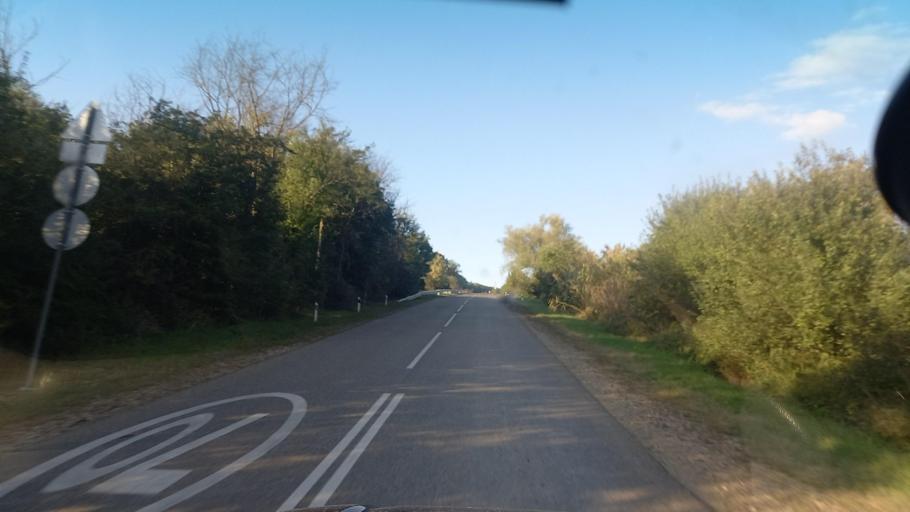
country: RU
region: Krasnodarskiy
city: Krymsk
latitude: 44.8926
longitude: 37.8971
